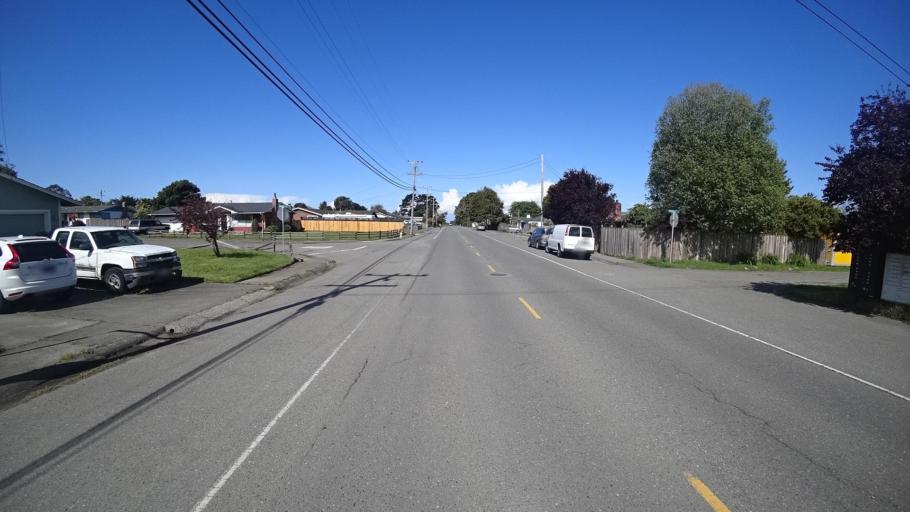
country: US
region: California
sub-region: Humboldt County
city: McKinleyville
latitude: 40.9416
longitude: -124.1123
